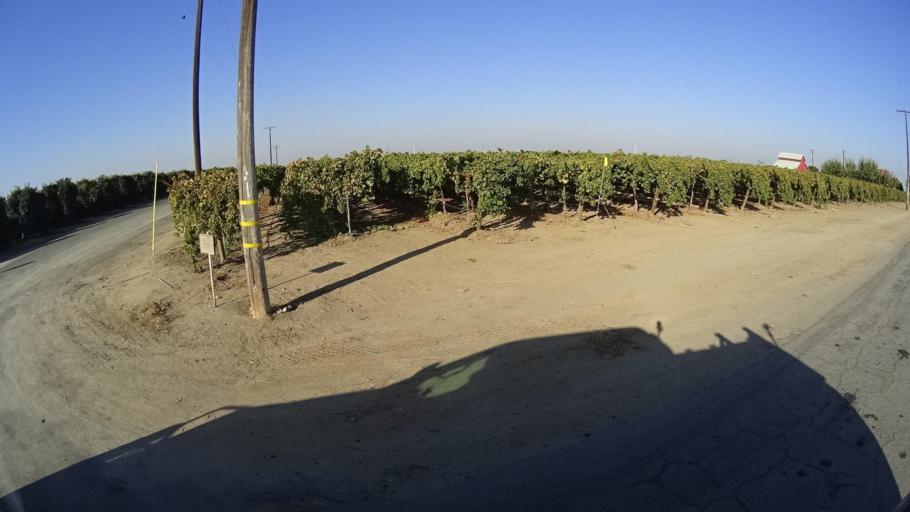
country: US
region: California
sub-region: Tulare County
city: Richgrove
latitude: 35.7688
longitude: -119.1518
